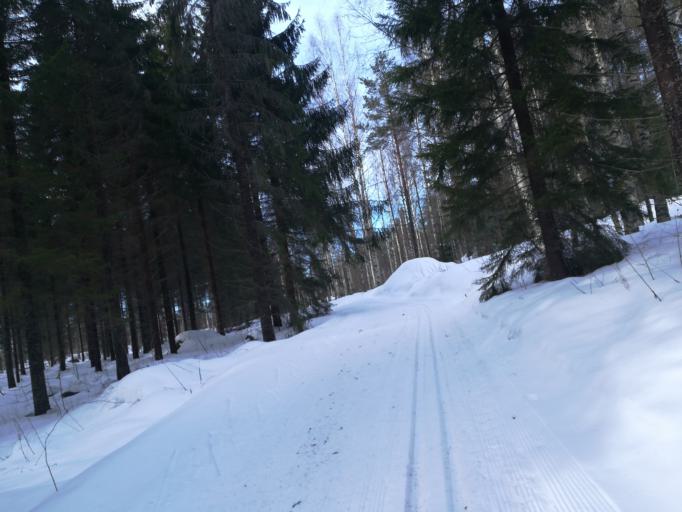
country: FI
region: Southern Savonia
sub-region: Savonlinna
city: Savonlinna
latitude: 61.8070
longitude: 29.0552
